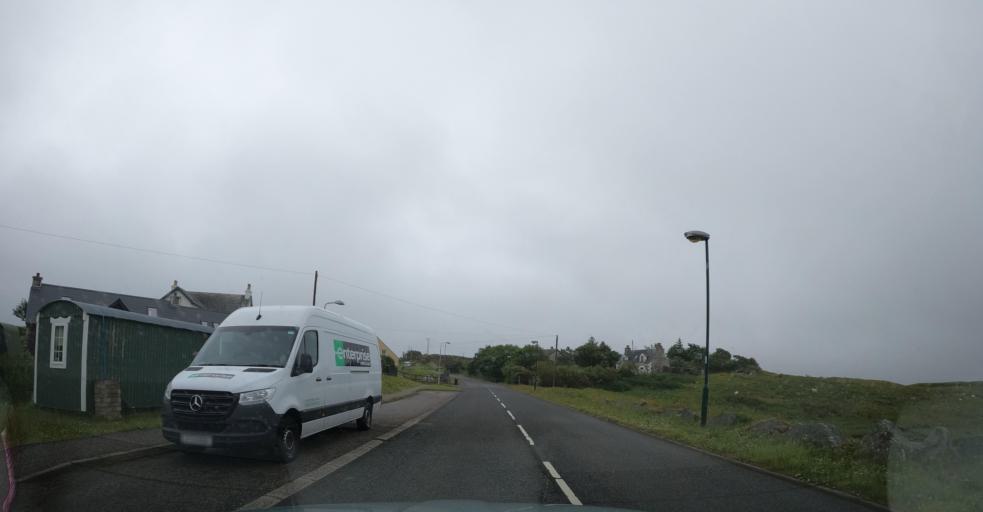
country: GB
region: Scotland
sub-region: Eilean Siar
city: Isle of North Uist
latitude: 57.6035
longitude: -7.1689
